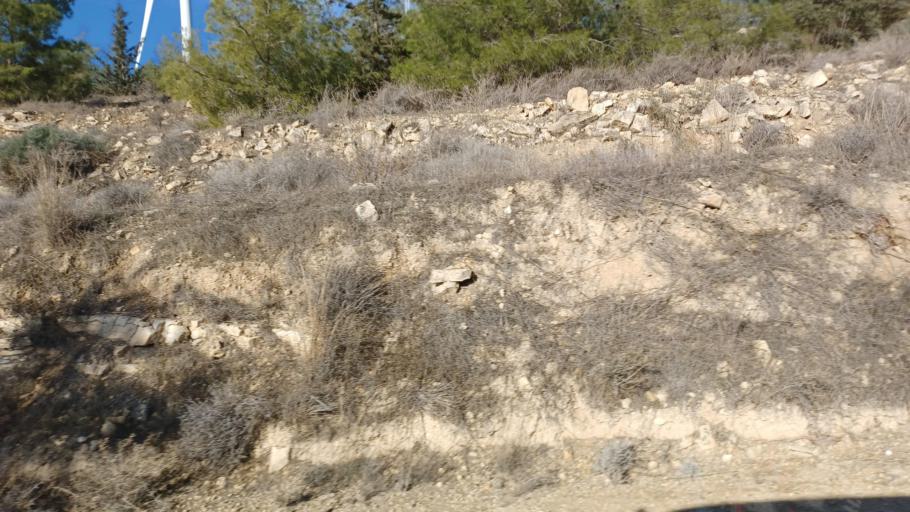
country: CY
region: Larnaka
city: Psevdas
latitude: 34.9547
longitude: 33.5059
